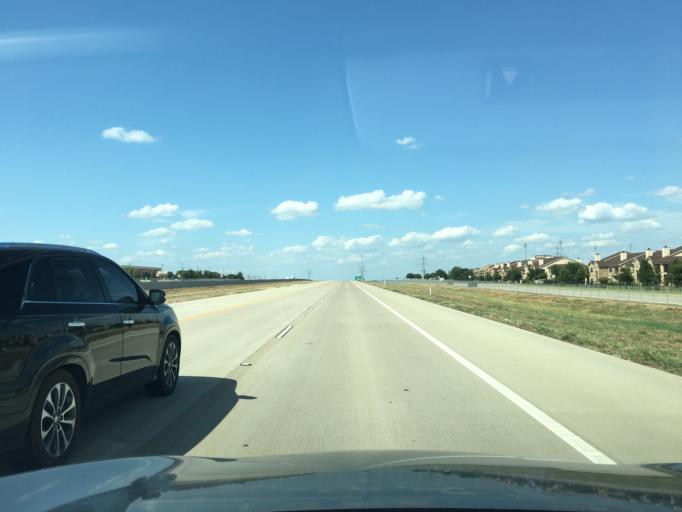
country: US
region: Texas
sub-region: Tarrant County
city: Mansfield
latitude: 32.5698
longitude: -97.0824
